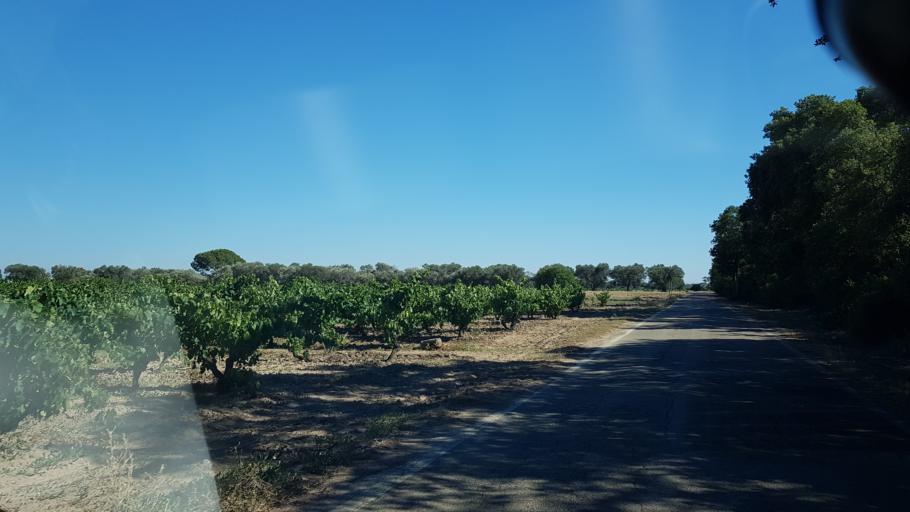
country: IT
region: Apulia
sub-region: Provincia di Brindisi
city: Tuturano
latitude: 40.5660
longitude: 17.8877
